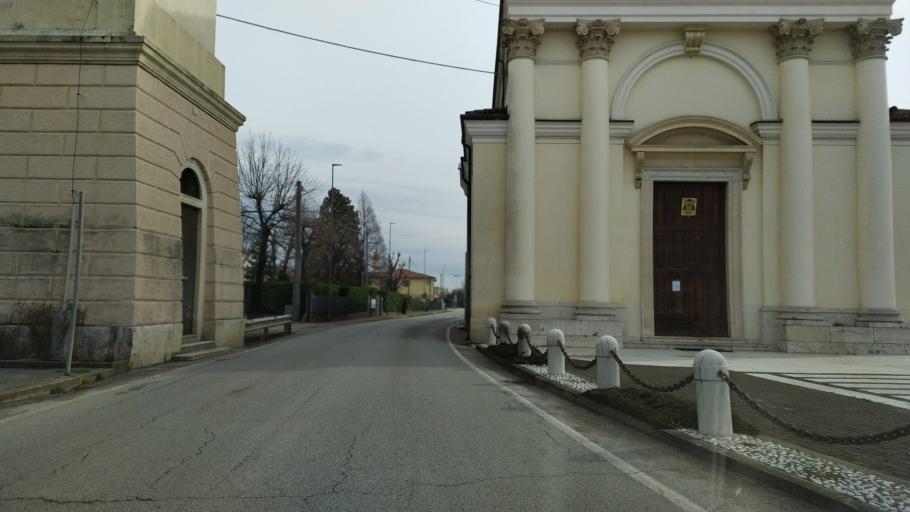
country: IT
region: Veneto
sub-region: Provincia di Vicenza
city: Novoledo
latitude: 45.6453
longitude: 11.5080
